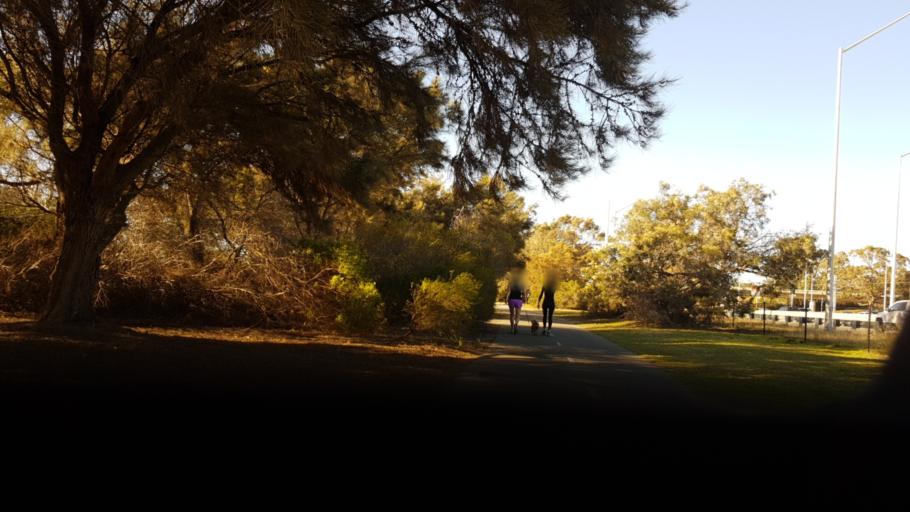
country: AU
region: Western Australia
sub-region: South Perth
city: Manning
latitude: -32.0157
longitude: 115.8564
